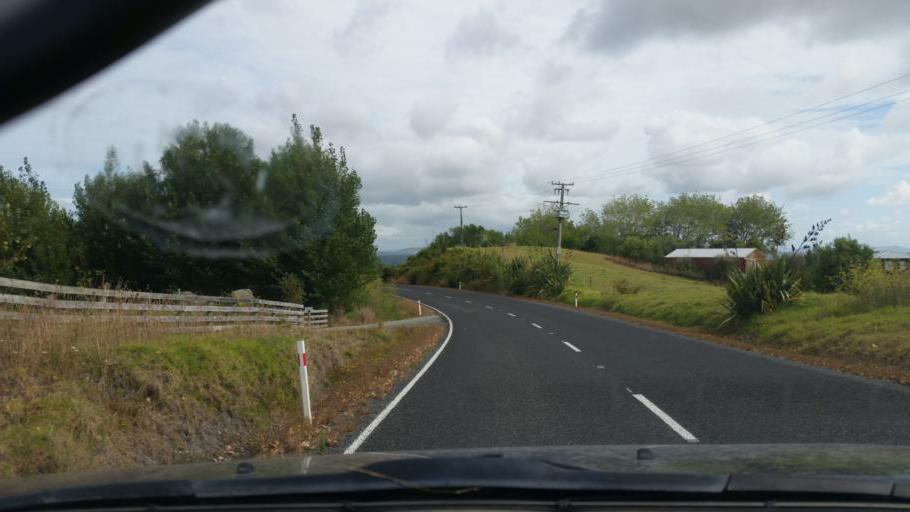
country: NZ
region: Northland
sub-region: Kaipara District
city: Dargaville
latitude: -35.9523
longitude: 173.9213
